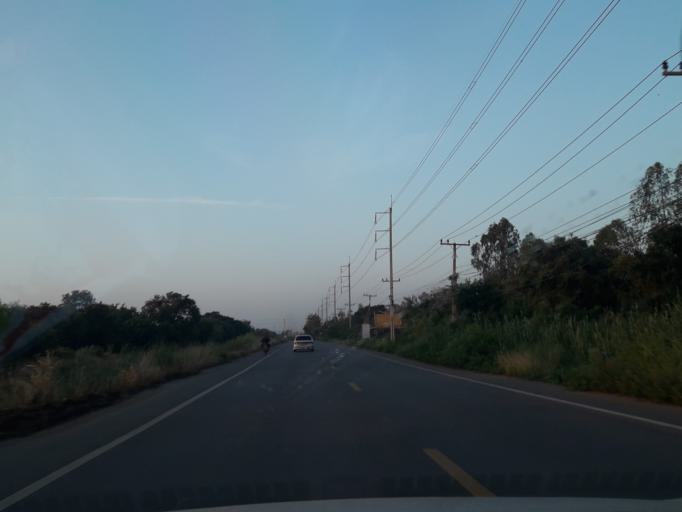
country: TH
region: Phra Nakhon Si Ayutthaya
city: Bang Pahan
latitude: 14.4786
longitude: 100.5548
